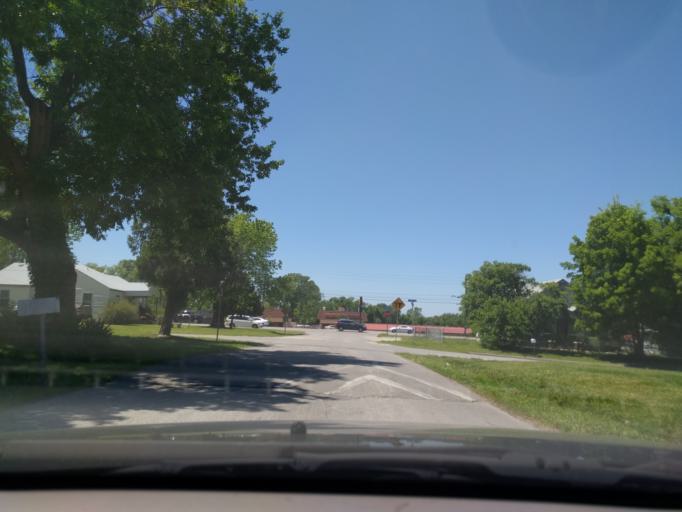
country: US
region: Oklahoma
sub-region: Tulsa County
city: Broken Arrow
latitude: 36.0535
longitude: -95.7965
